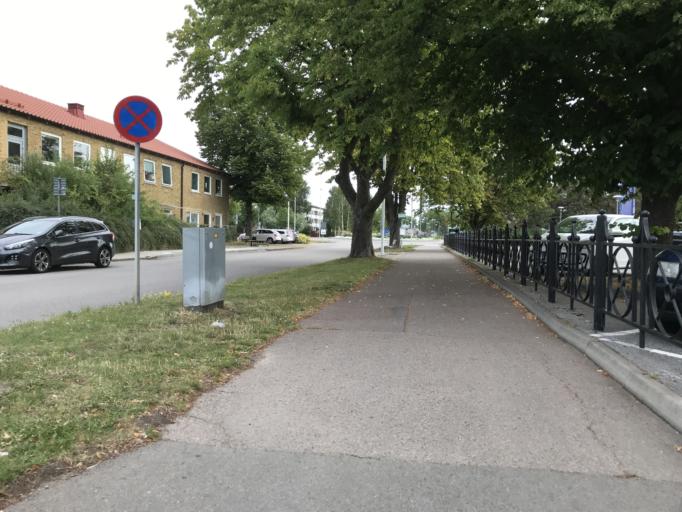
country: SE
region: Skane
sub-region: Landskrona
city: Landskrona
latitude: 55.8845
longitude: 12.8392
